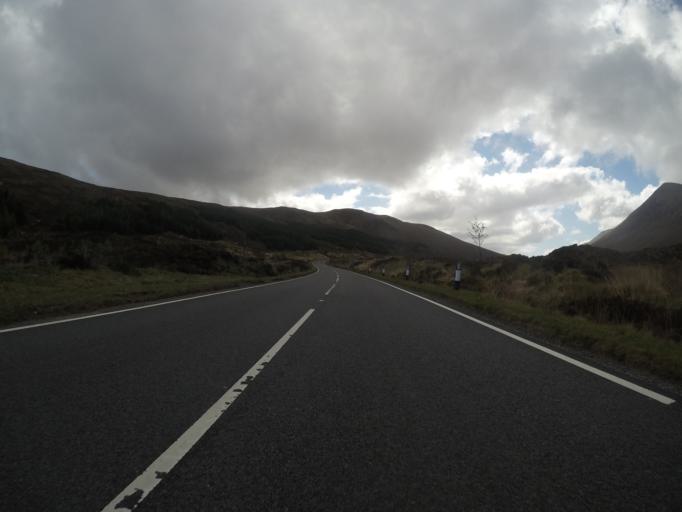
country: GB
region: Scotland
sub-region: Highland
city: Portree
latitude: 57.2989
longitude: -6.0892
